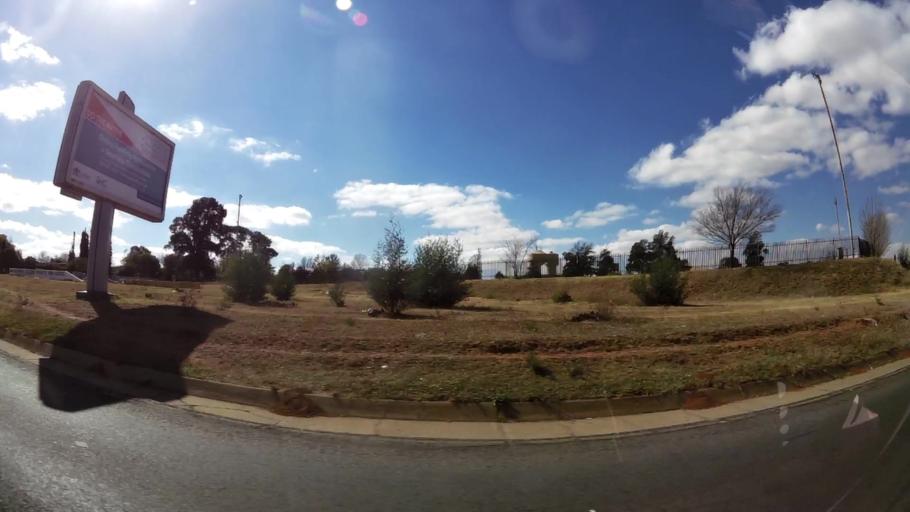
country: ZA
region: Gauteng
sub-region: West Rand District Municipality
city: Krugersdorp
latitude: -26.1075
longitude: 27.8021
